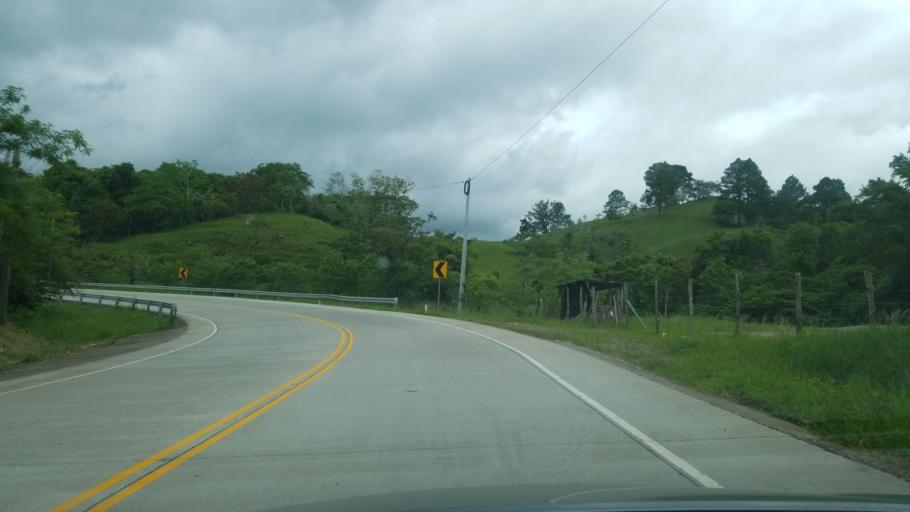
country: HN
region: Copan
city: San Jeronimo
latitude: 14.9466
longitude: -88.9145
